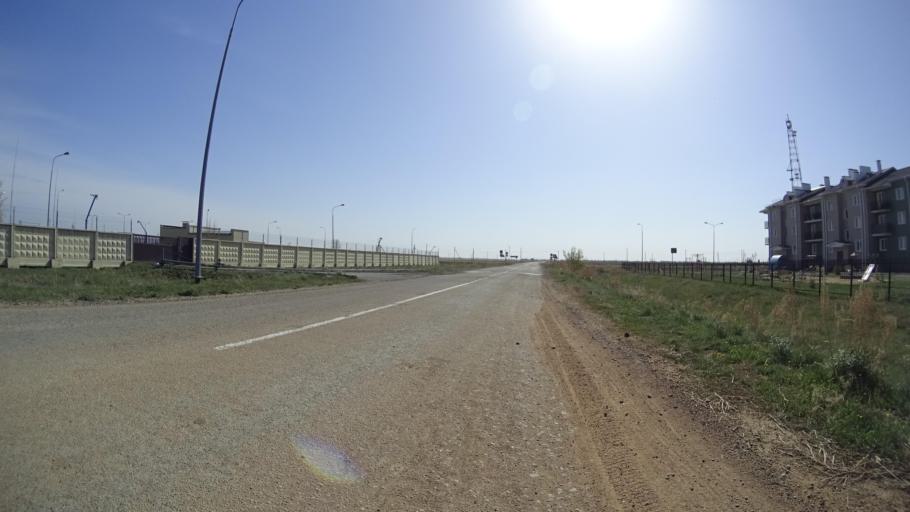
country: RU
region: Chelyabinsk
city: Chesma
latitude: 53.7924
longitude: 61.0415
